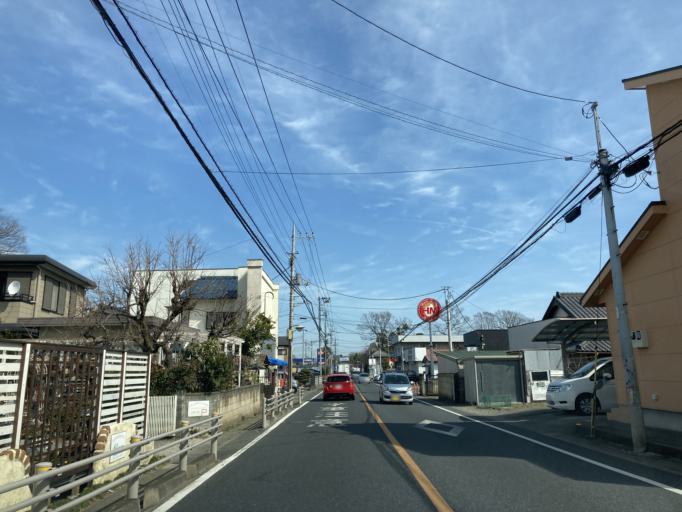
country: JP
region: Saitama
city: Tokorozawa
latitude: 35.8133
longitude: 139.4812
